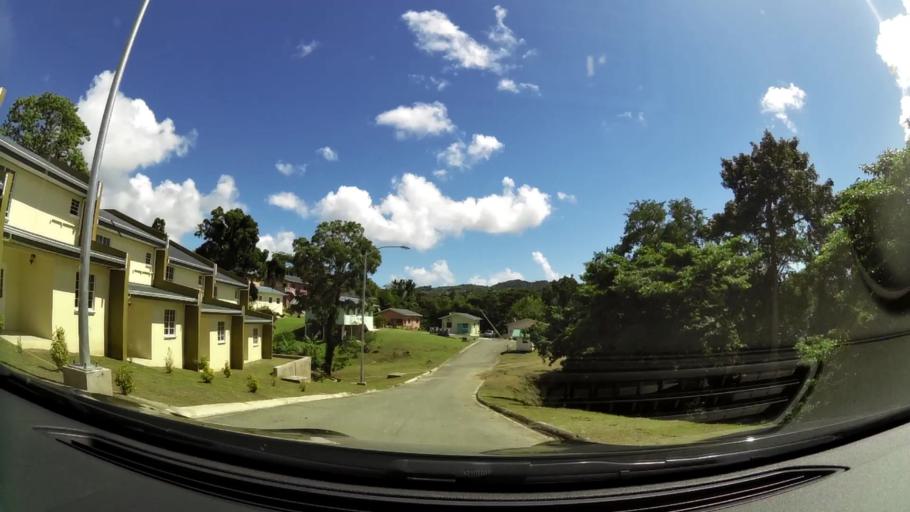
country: TT
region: Tobago
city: Scarborough
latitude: 11.2187
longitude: -60.7717
